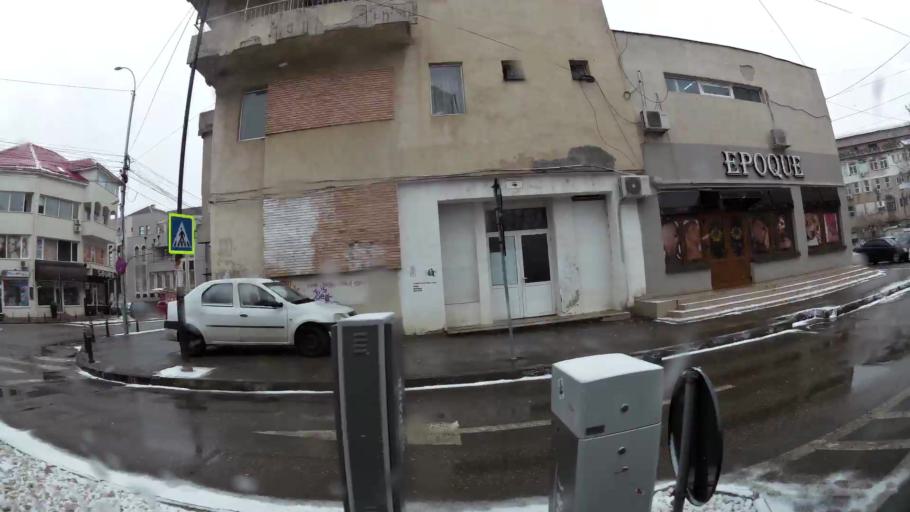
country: RO
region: Dambovita
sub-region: Municipiul Targoviste
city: Targoviste
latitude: 44.9279
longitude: 25.4601
